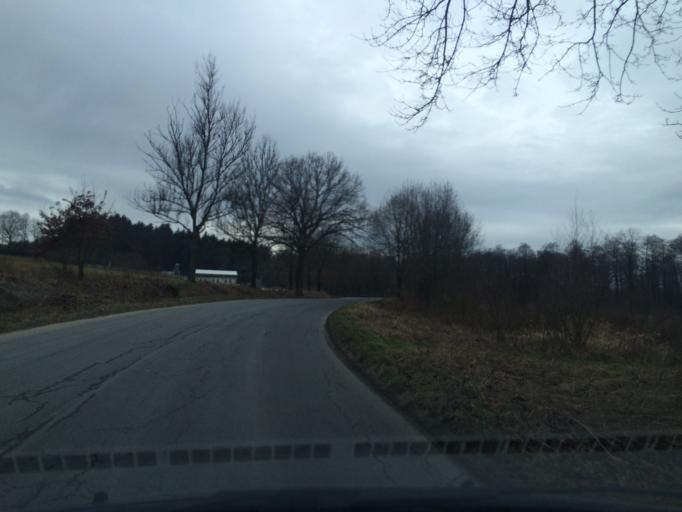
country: PL
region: Lower Silesian Voivodeship
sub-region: Powiat lwowecki
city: Lwowek Slaski
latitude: 51.1198
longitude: 15.5259
